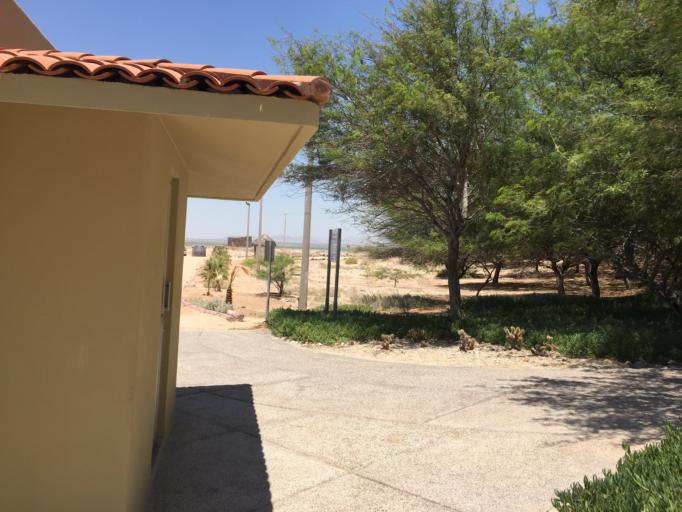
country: MX
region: Sonora
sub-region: Puerto Penasco
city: Puerto Penasco
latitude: 31.2453
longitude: -113.2649
